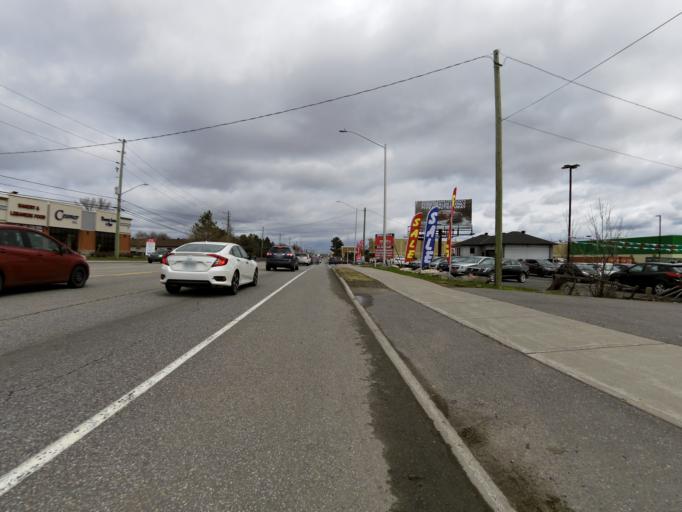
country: CA
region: Ontario
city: Ottawa
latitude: 45.4500
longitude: -75.5188
